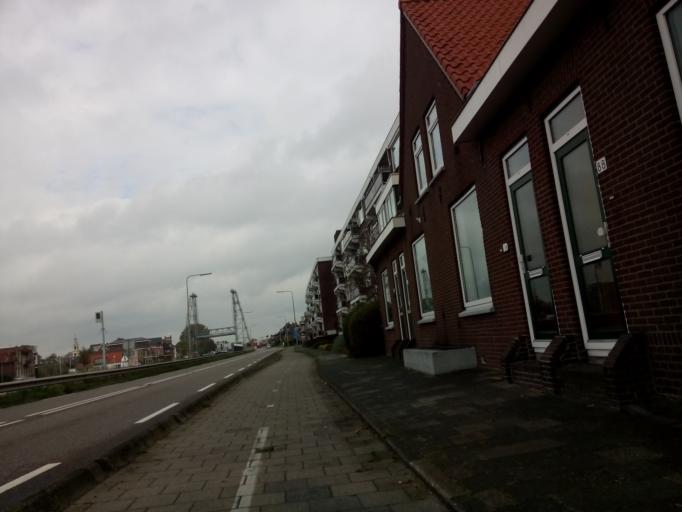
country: NL
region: South Holland
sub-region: Gemeente Waddinxveen
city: Waddinxveen
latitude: 52.0401
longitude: 4.6594
